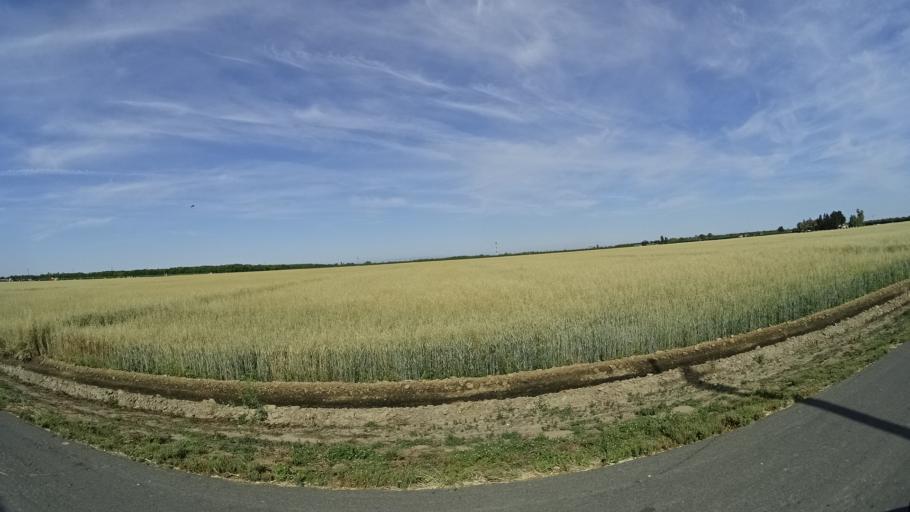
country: US
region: California
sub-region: Kings County
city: Hanford
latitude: 36.3672
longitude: -119.6100
